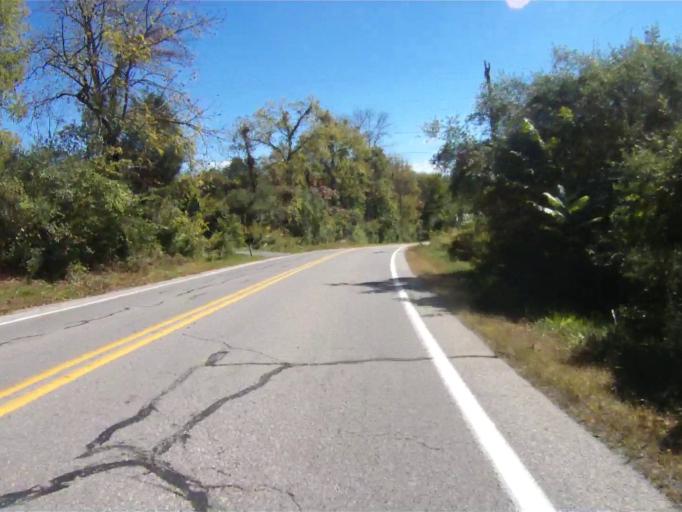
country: US
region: Pennsylvania
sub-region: Centre County
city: Park Forest Village
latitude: 40.8691
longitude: -77.8905
